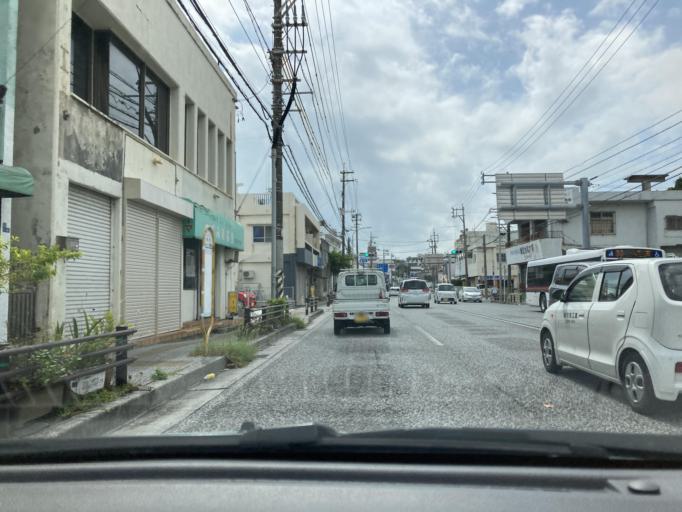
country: JP
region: Okinawa
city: Okinawa
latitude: 26.3249
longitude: 127.8228
